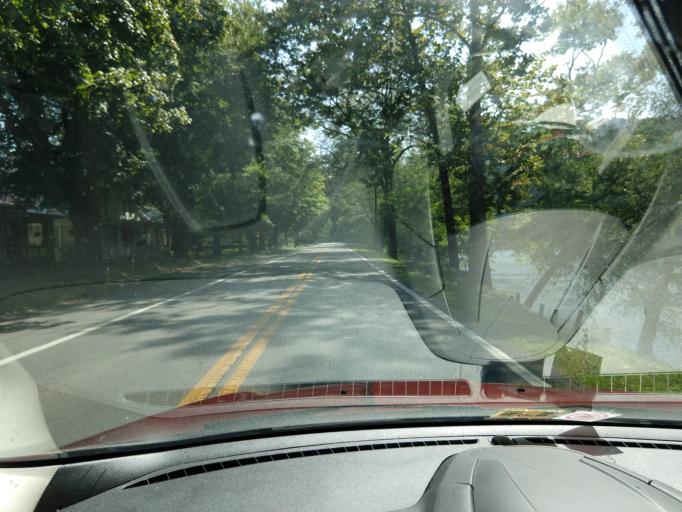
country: US
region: West Virginia
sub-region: Greenbrier County
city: Alderson
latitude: 37.7247
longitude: -80.6357
